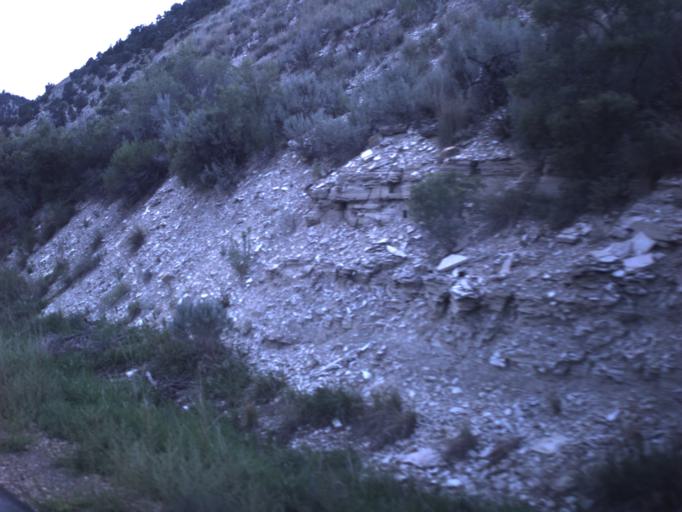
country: US
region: Utah
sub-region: Duchesne County
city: Duchesne
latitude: 40.0553
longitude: -110.5222
